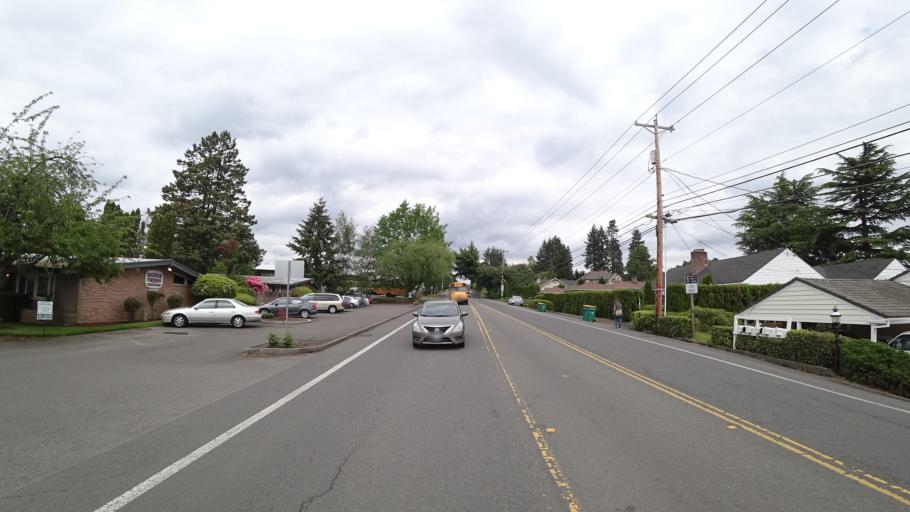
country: US
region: Oregon
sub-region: Washington County
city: Raleigh Hills
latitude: 45.4813
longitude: -122.7595
